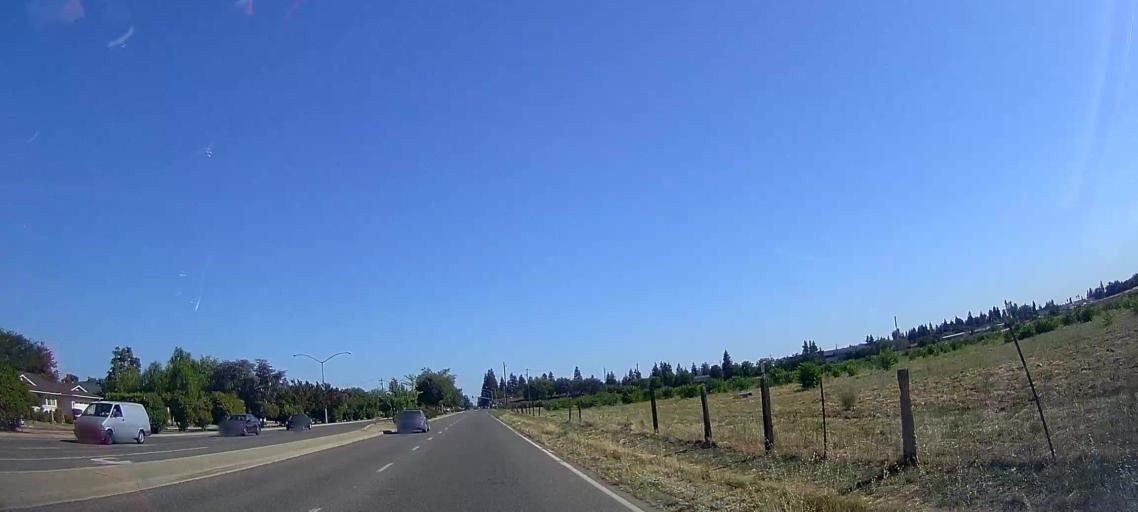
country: US
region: California
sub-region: Fresno County
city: Clovis
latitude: 36.8335
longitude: -119.7814
